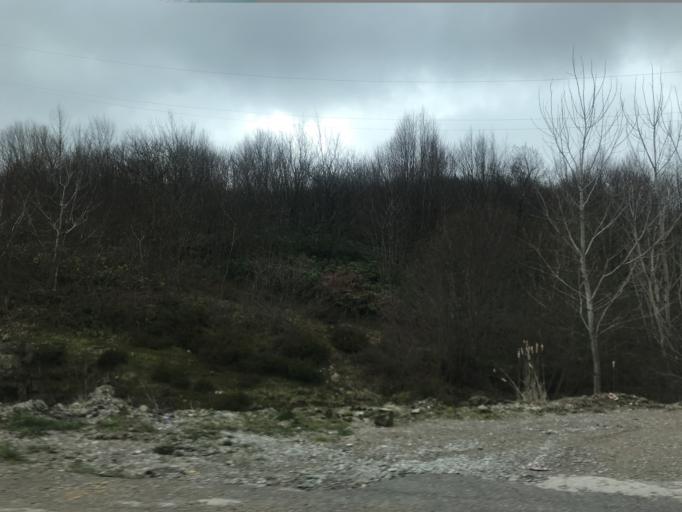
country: TR
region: Bartin
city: Amasra
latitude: 41.7172
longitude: 32.3955
